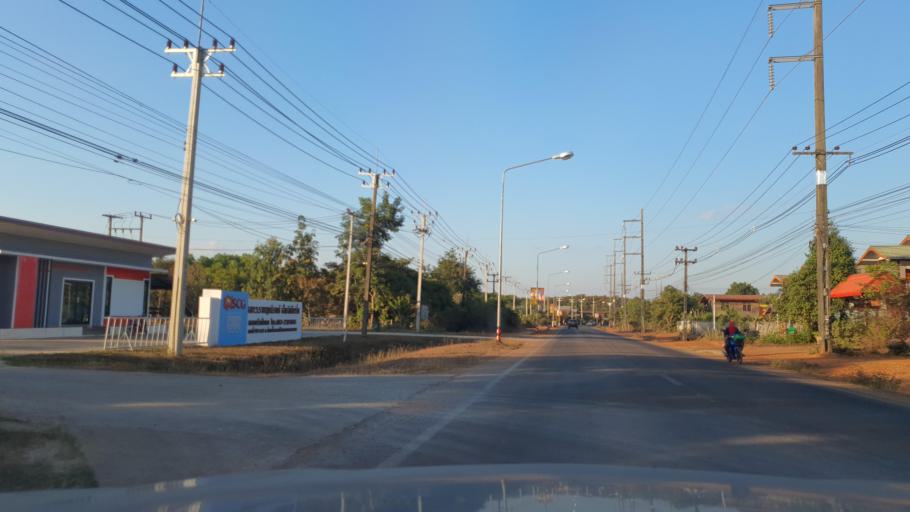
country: TH
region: Nakhon Phanom
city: Si Songkhram
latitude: 17.5833
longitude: 104.2331
